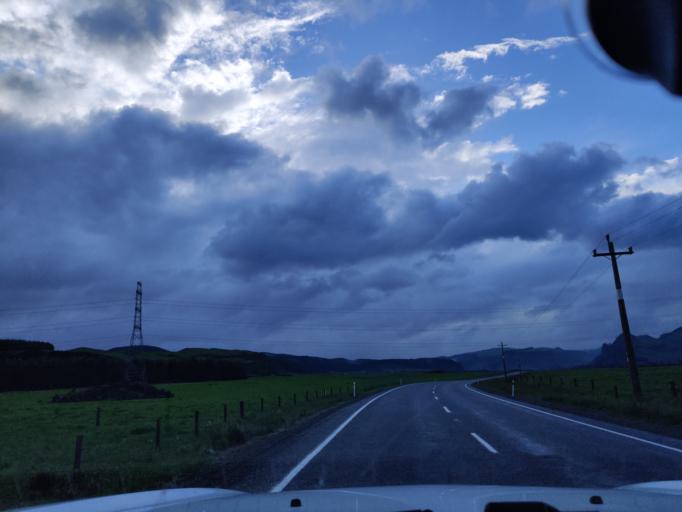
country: NZ
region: Waikato
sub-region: South Waikato District
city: Tokoroa
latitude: -38.3955
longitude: 175.7848
